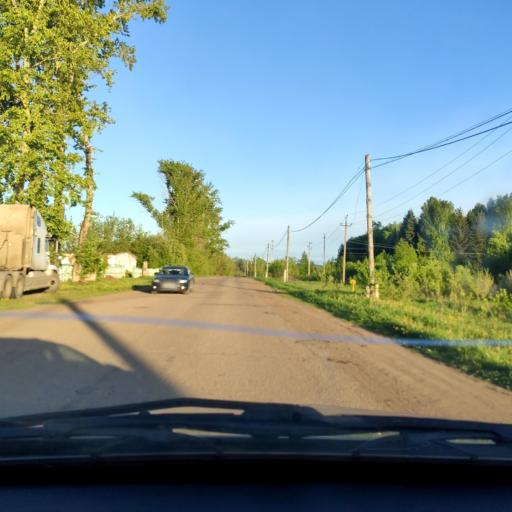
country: RU
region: Bashkortostan
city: Yazykovo
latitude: 55.0436
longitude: 56.1856
